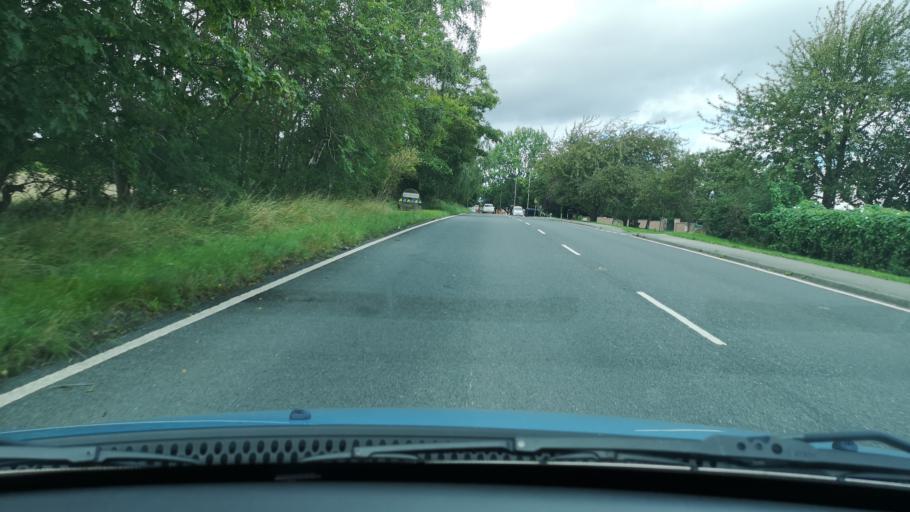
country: GB
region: England
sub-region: City and Borough of Wakefield
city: Low Ackworth
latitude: 53.6385
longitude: -1.3295
